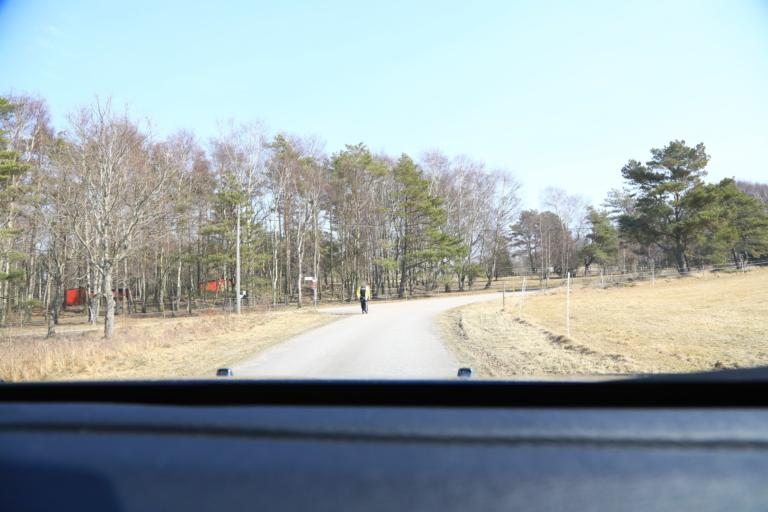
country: SE
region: Halland
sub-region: Kungsbacka Kommun
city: Frillesas
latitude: 57.2655
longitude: 12.1410
